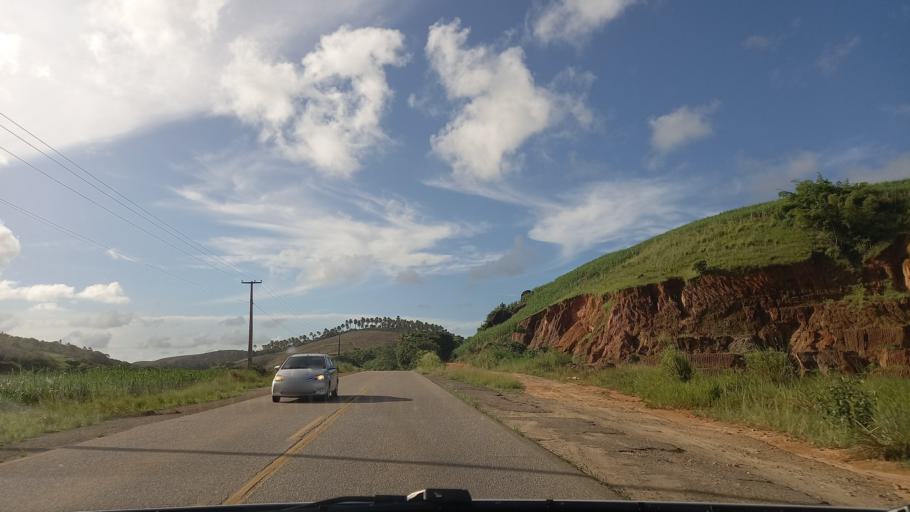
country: BR
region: Pernambuco
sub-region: Sirinhaem
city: Sirinhaem
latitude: -8.6351
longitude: -35.1191
